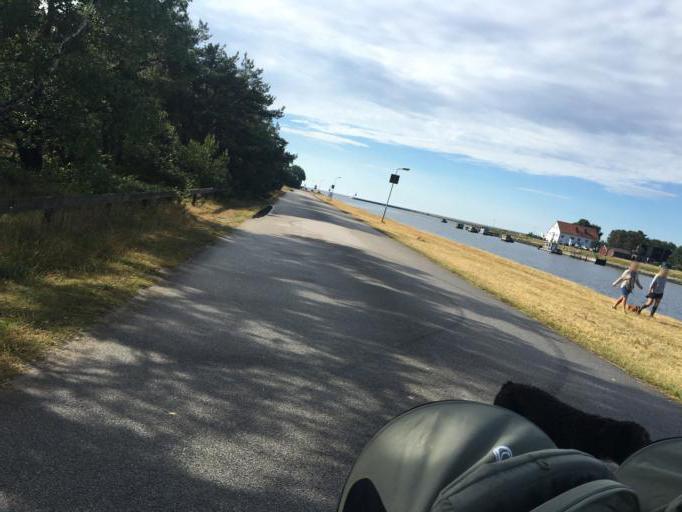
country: SE
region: Skane
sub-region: Vellinge Kommun
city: Hollviken
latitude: 55.4005
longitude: 12.9437
